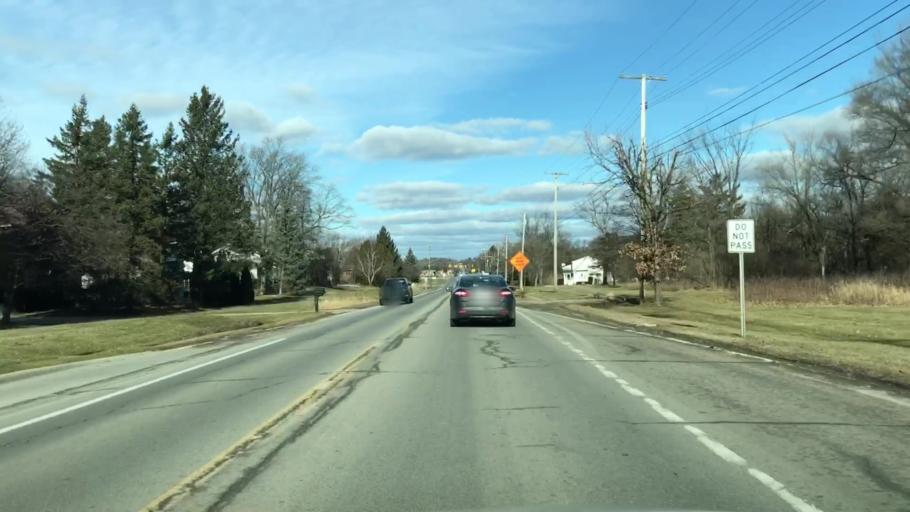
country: US
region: Michigan
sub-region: Oakland County
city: Auburn Hills
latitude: 42.6904
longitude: -83.1944
